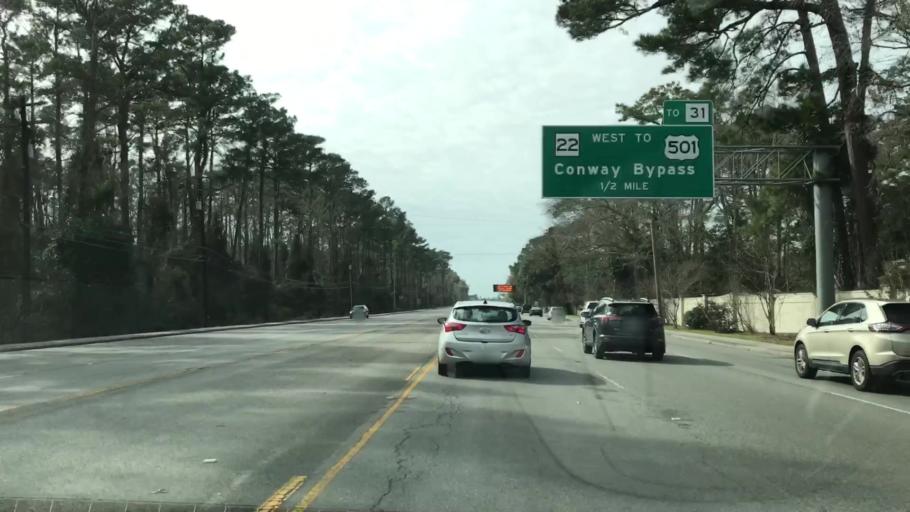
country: US
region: South Carolina
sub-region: Horry County
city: North Myrtle Beach
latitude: 33.7932
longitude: -78.7567
